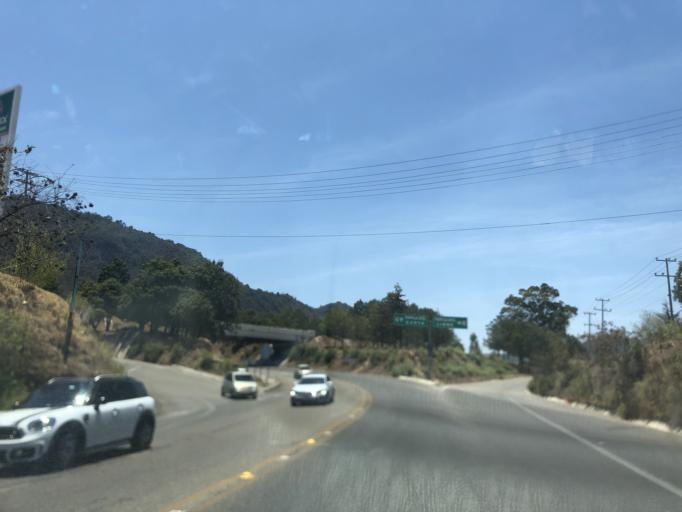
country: MX
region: Chiapas
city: San Cristobal de las Casas
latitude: 16.7220
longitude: -92.6529
